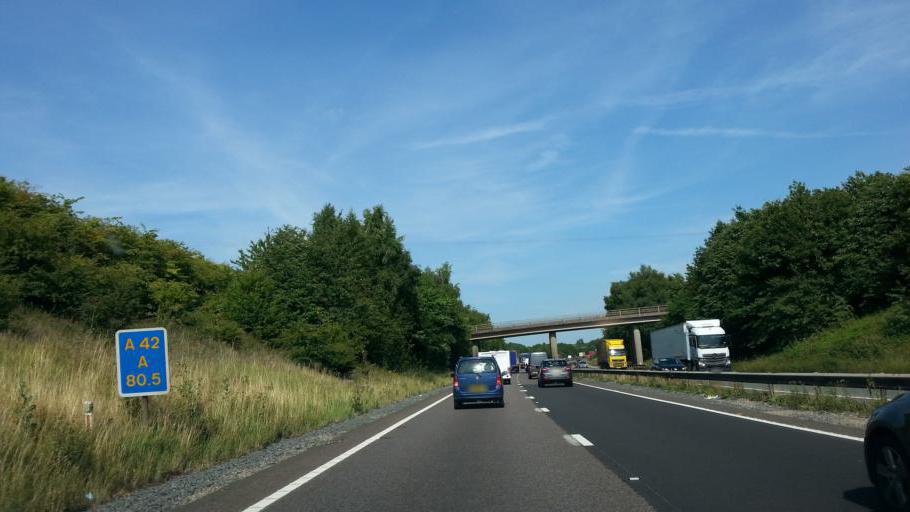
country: GB
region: England
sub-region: Derbyshire
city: Melbourne
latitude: 52.7960
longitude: -1.3947
